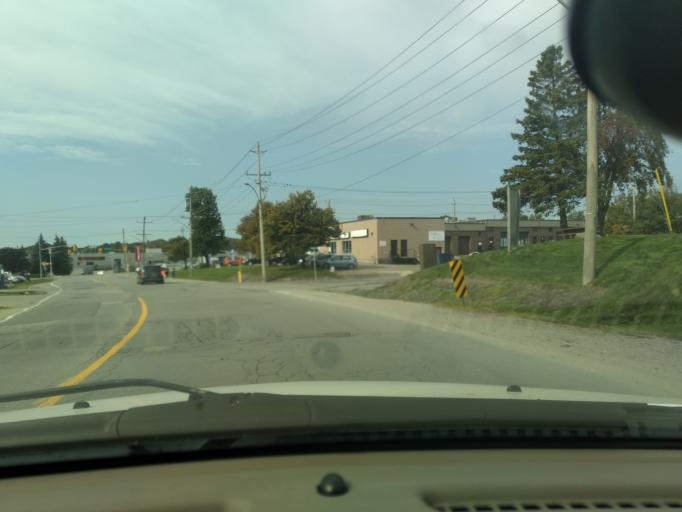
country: CA
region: Ontario
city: Barrie
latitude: 44.4078
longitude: -79.6838
